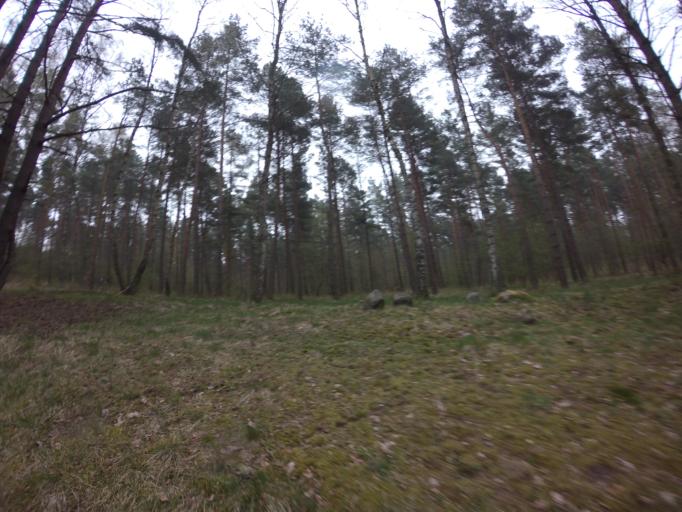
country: PL
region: West Pomeranian Voivodeship
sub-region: Powiat choszczenski
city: Recz
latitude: 53.1855
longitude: 15.5293
